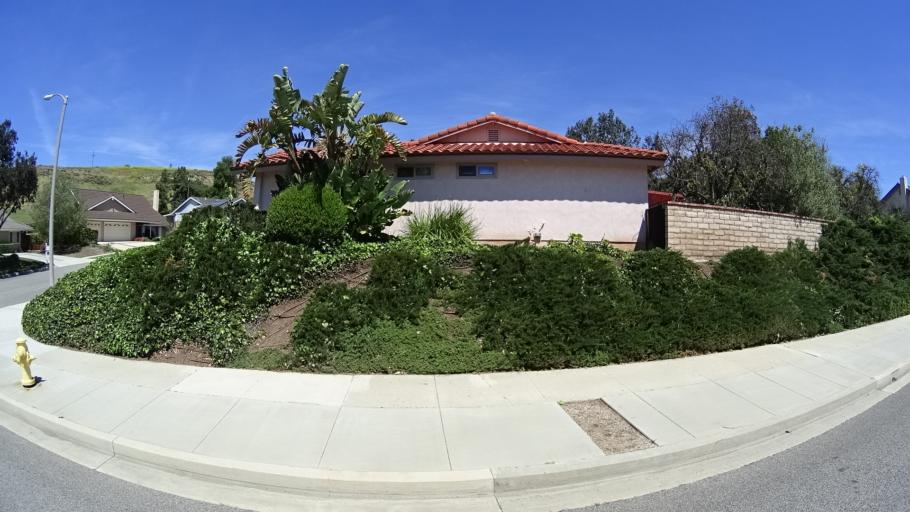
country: US
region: California
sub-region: Ventura County
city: Moorpark
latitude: 34.2324
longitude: -118.8749
